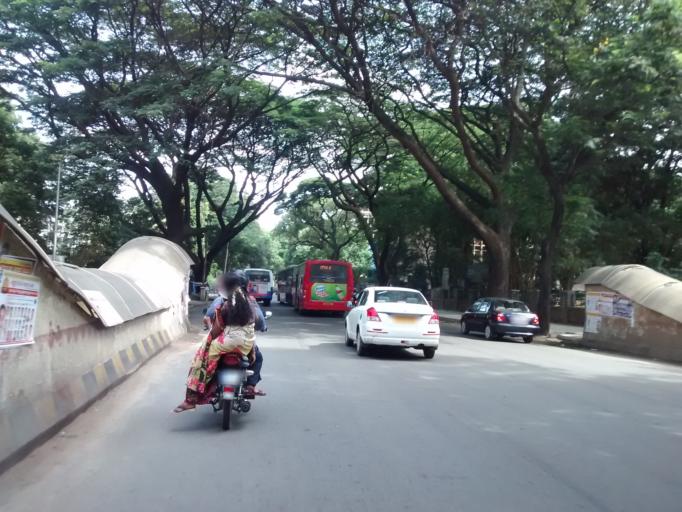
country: IN
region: Karnataka
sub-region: Bangalore Urban
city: Bangalore
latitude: 12.9739
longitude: 77.5866
